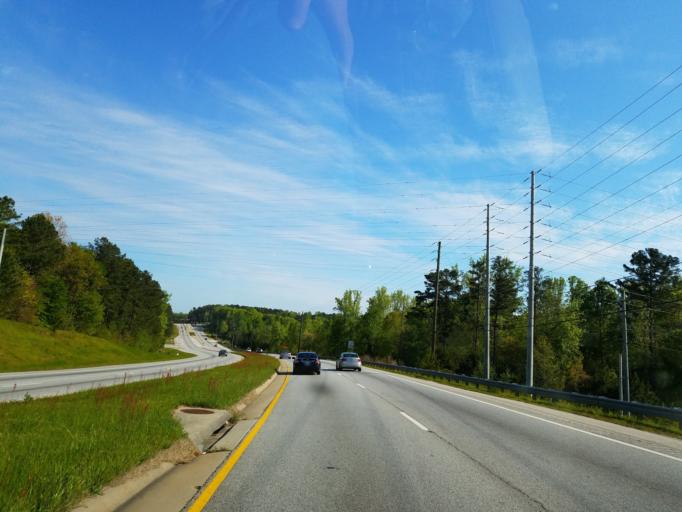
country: US
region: Georgia
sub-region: Douglas County
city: Lithia Springs
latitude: 33.7098
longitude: -84.6628
